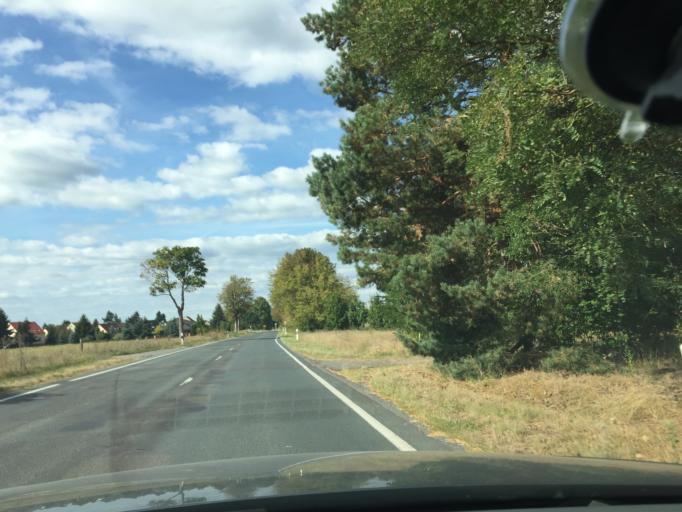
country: DE
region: Brandenburg
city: Spreenhagen
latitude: 52.3555
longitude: 13.8519
